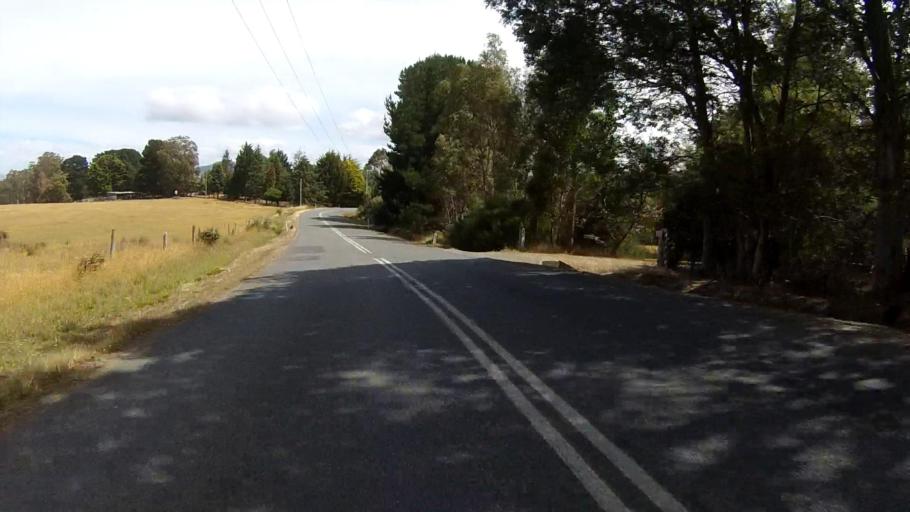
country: AU
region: Tasmania
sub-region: Huon Valley
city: Cygnet
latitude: -43.2172
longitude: 147.1227
